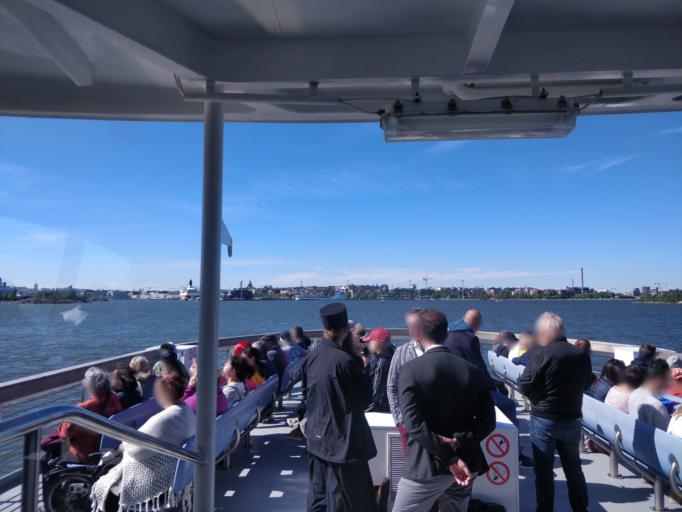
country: FI
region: Uusimaa
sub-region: Helsinki
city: Helsinki
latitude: 60.1569
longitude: 24.9825
